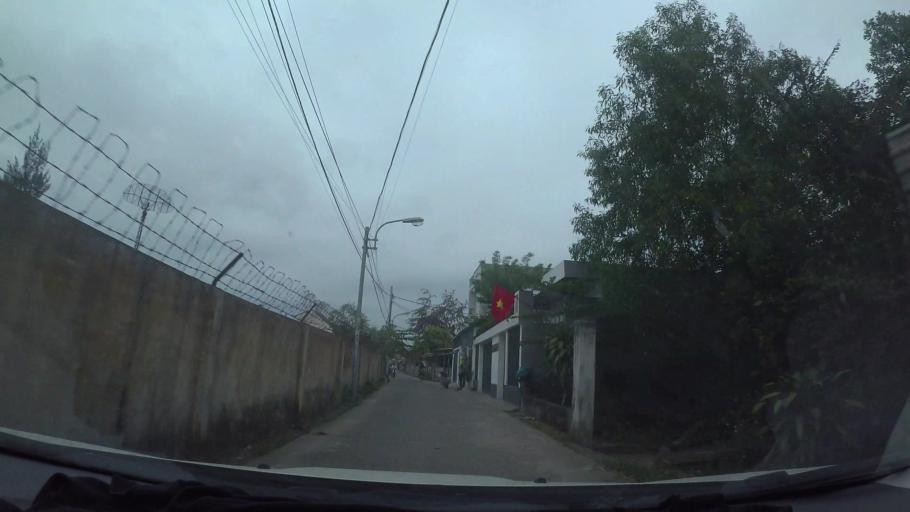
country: VN
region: Da Nang
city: Lien Chieu
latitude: 16.0844
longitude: 108.1542
